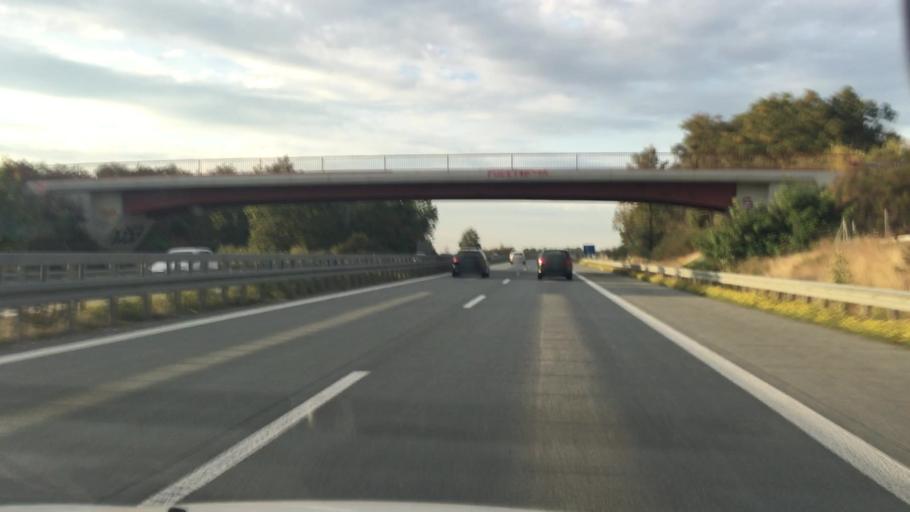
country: DE
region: Saxony
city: Schonfeld
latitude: 51.3207
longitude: 13.7212
